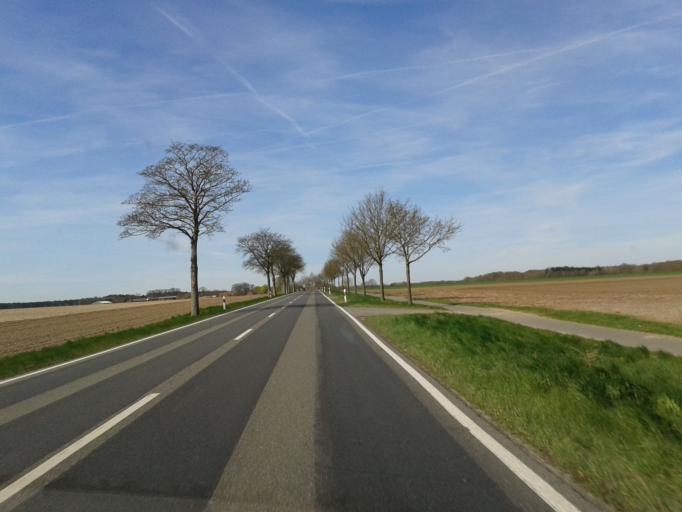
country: DE
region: Lower Saxony
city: Gerdau
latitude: 52.9603
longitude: 10.4478
